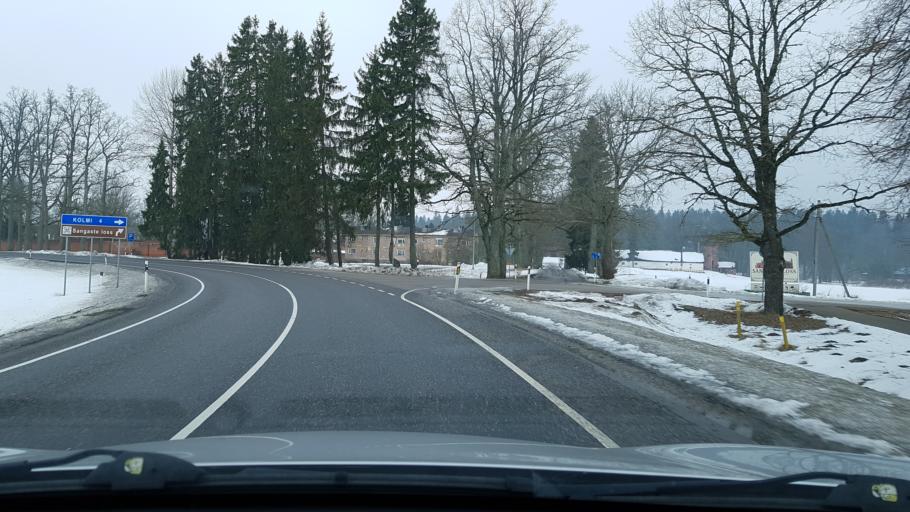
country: EE
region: Vorumaa
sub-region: Antsla vald
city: Vana-Antsla
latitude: 57.9044
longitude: 26.2863
